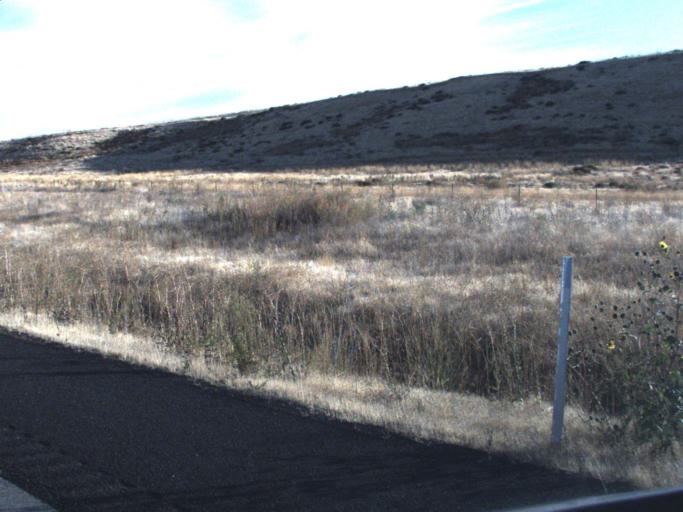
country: US
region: Washington
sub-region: Franklin County
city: Connell
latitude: 46.6828
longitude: -118.8415
